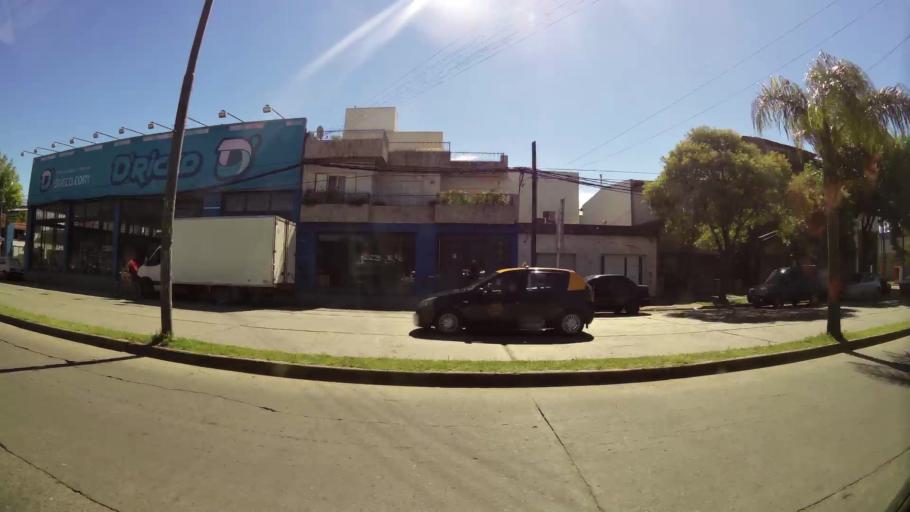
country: AR
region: Santa Fe
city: Granadero Baigorria
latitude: -32.9319
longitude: -60.7131
